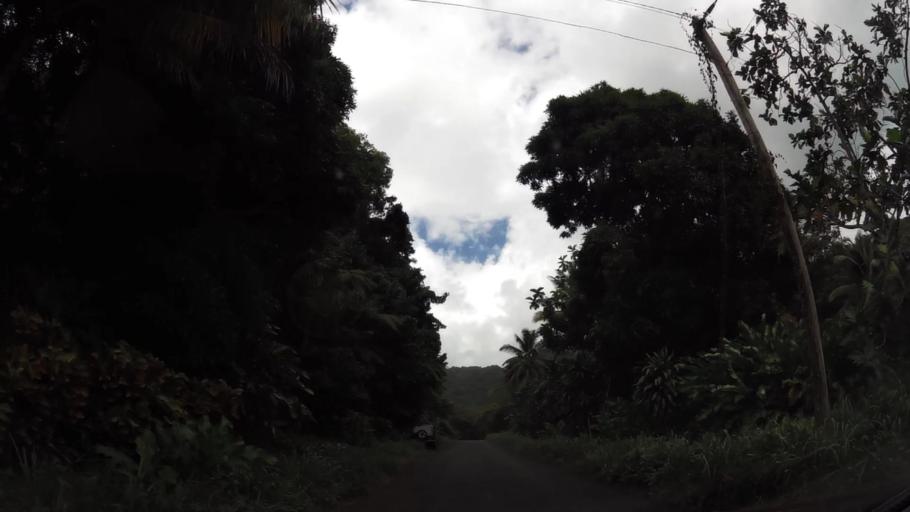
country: DM
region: Saint David
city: Castle Bruce
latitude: 15.4434
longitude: -61.2635
